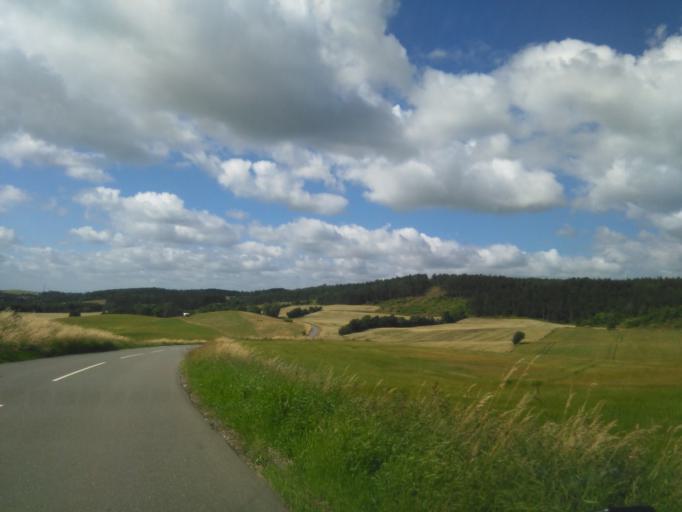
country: DK
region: Central Jutland
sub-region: Syddjurs Kommune
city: Ronde
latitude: 56.1981
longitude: 10.5127
